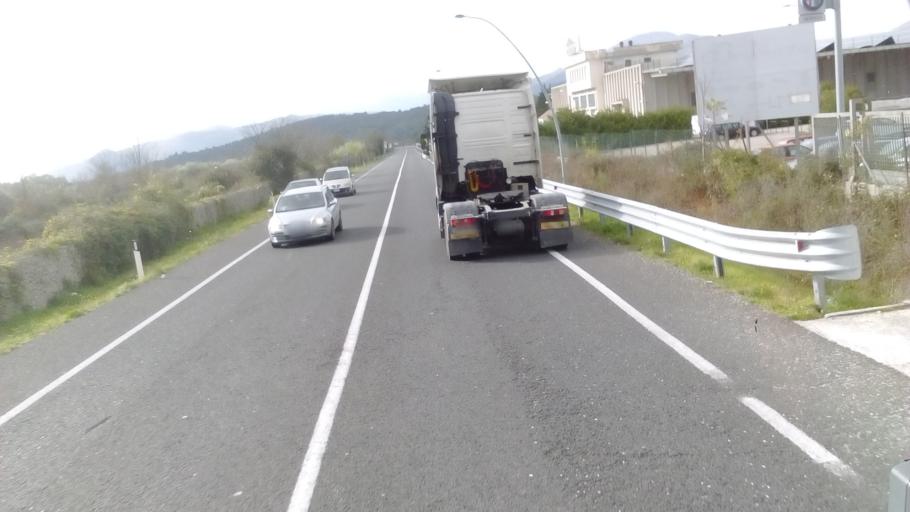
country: IT
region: Molise
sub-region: Provincia di Isernia
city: Macchia d'Isernia
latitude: 41.5628
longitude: 14.1870
